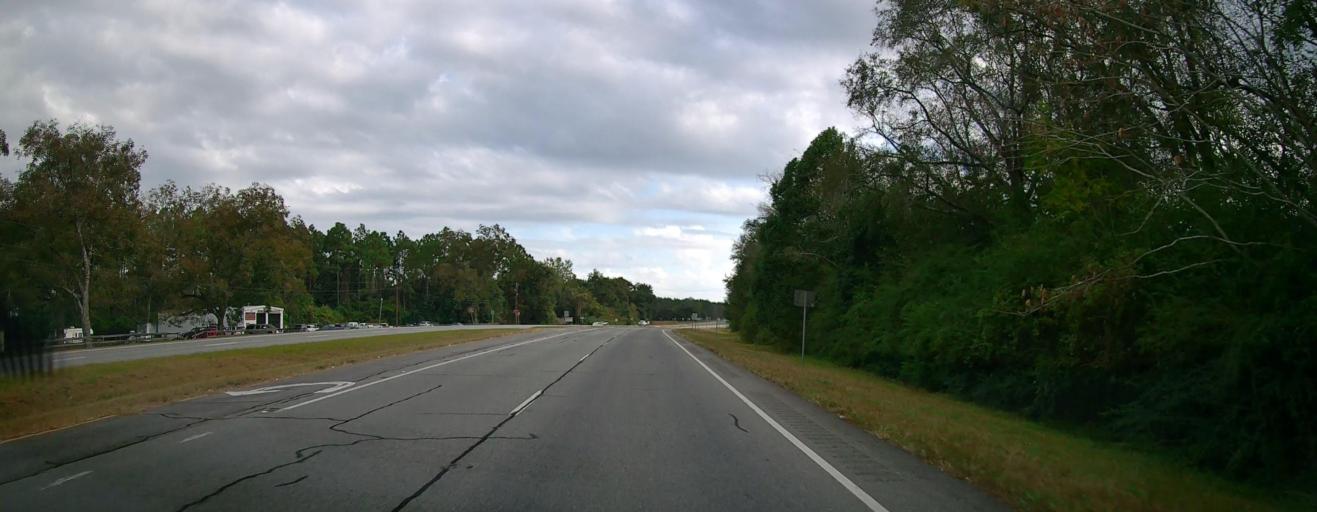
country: US
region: Georgia
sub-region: Thomas County
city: Meigs
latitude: 31.0796
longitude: -84.0820
